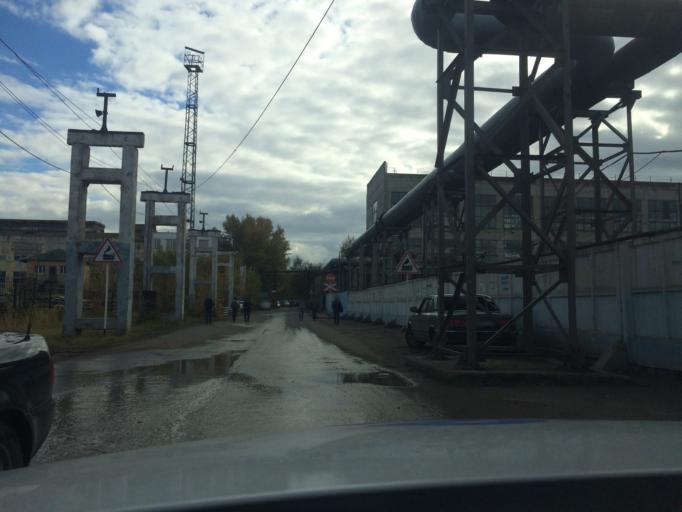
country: KZ
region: Astana Qalasy
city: Astana
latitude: 51.1833
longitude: 71.4316
